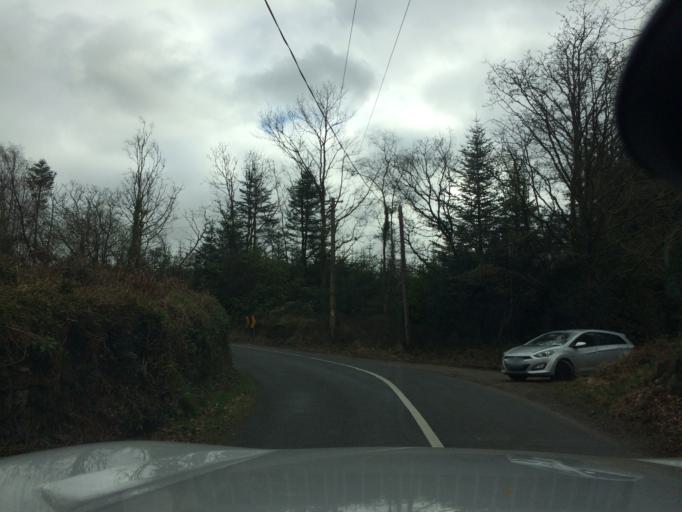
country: IE
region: Munster
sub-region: South Tipperary
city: Cluain Meala
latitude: 52.3434
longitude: -7.6372
